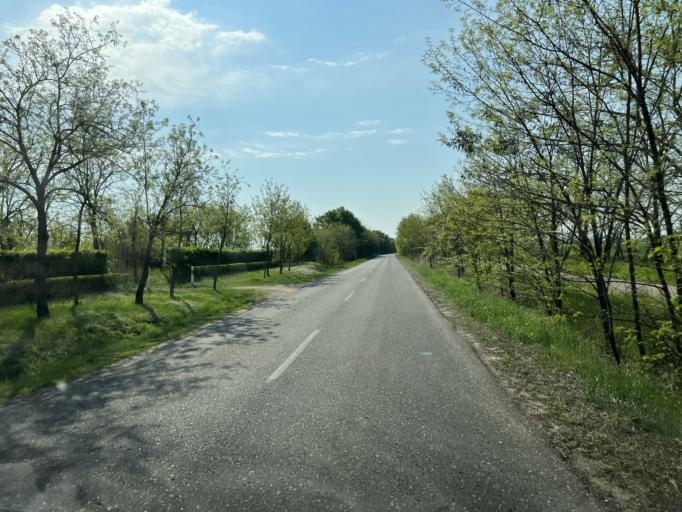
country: HU
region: Pest
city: Jaszkarajeno
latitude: 47.0841
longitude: 20.0375
